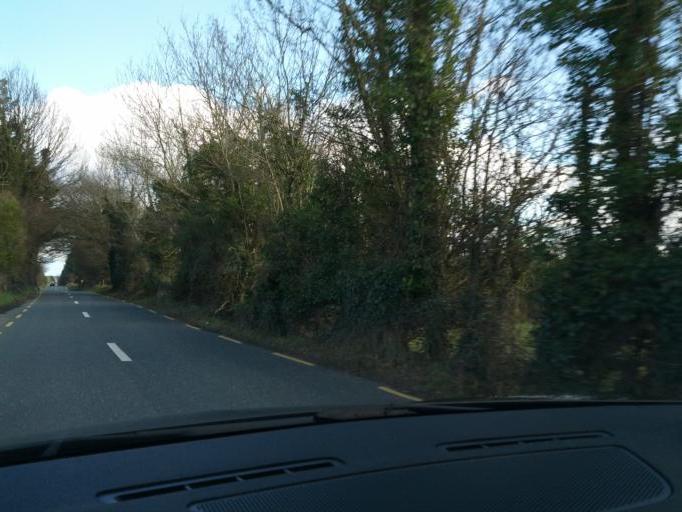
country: IE
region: Connaught
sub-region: Roscommon
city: Castlerea
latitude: 53.6436
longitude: -8.5434
